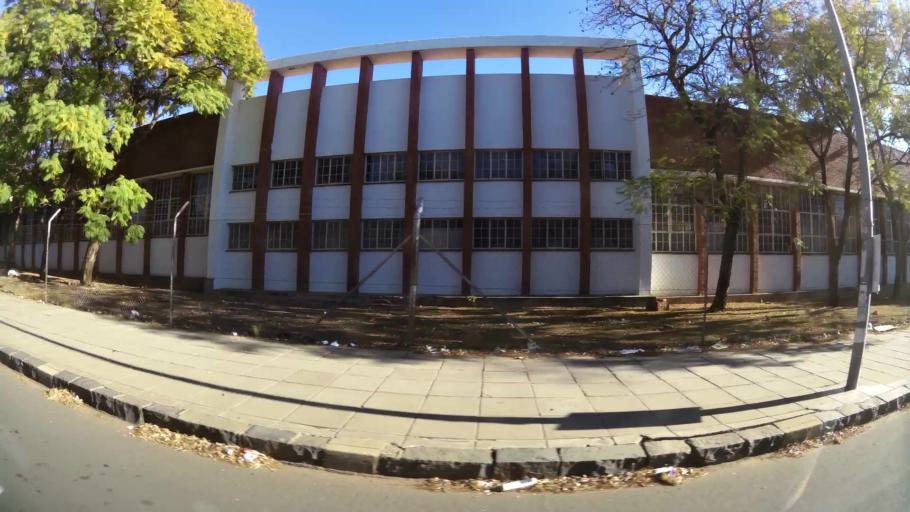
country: ZA
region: Northern Cape
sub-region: Frances Baard District Municipality
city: Kimberley
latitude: -28.7458
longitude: 24.7703
